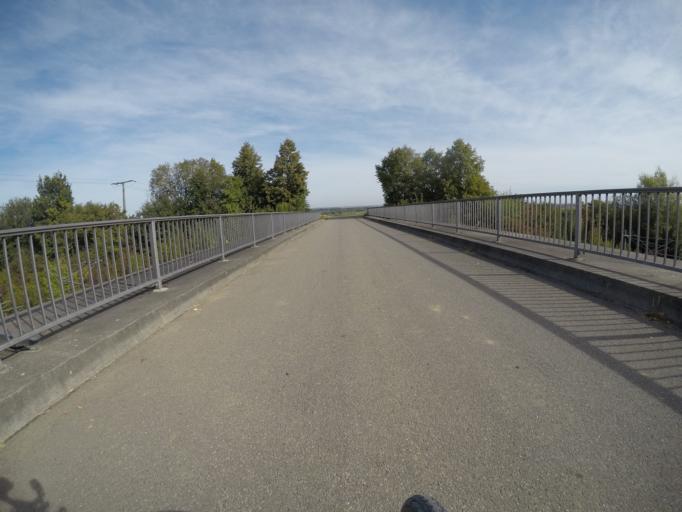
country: DE
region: Baden-Wuerttemberg
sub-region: Regierungsbezirk Stuttgart
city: Schwieberdingen
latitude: 48.8854
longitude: 9.0989
